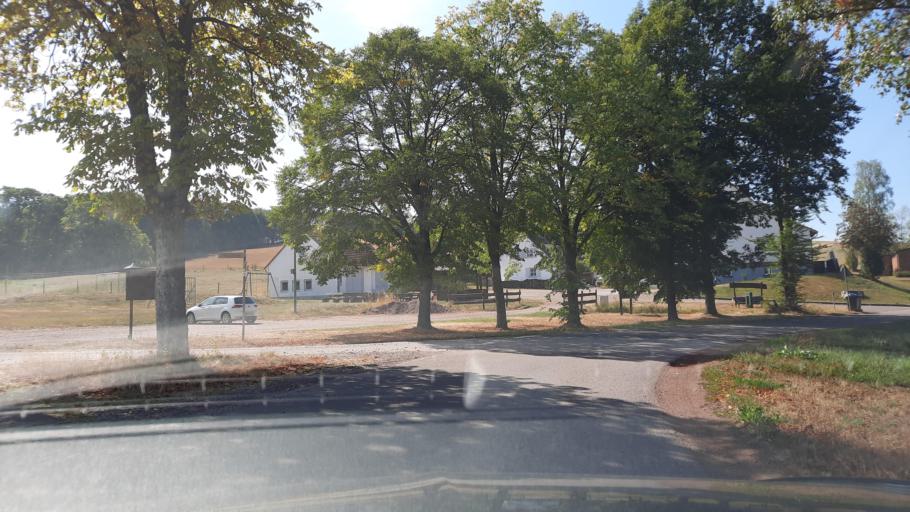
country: DE
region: Rheinland-Pfalz
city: Baldringen
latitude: 49.6092
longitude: 6.6631
